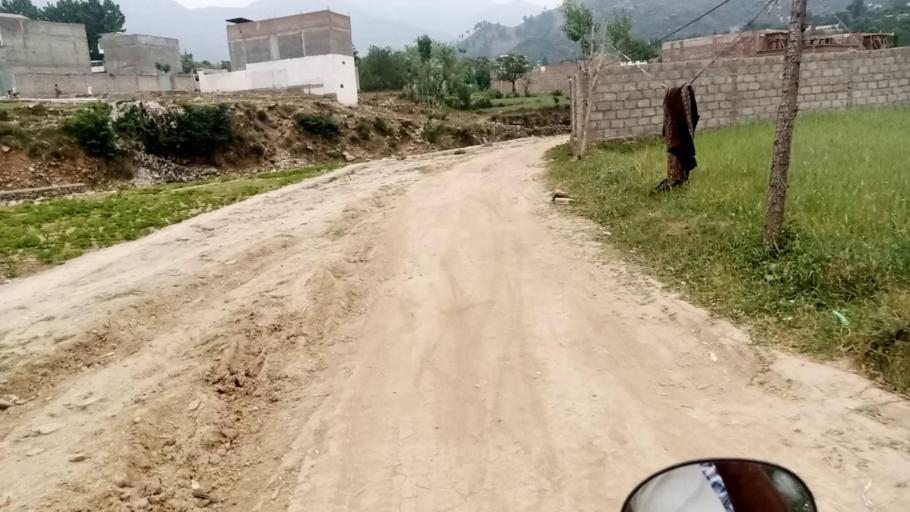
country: PK
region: Khyber Pakhtunkhwa
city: Saidu Sharif
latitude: 34.7542
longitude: 72.3865
